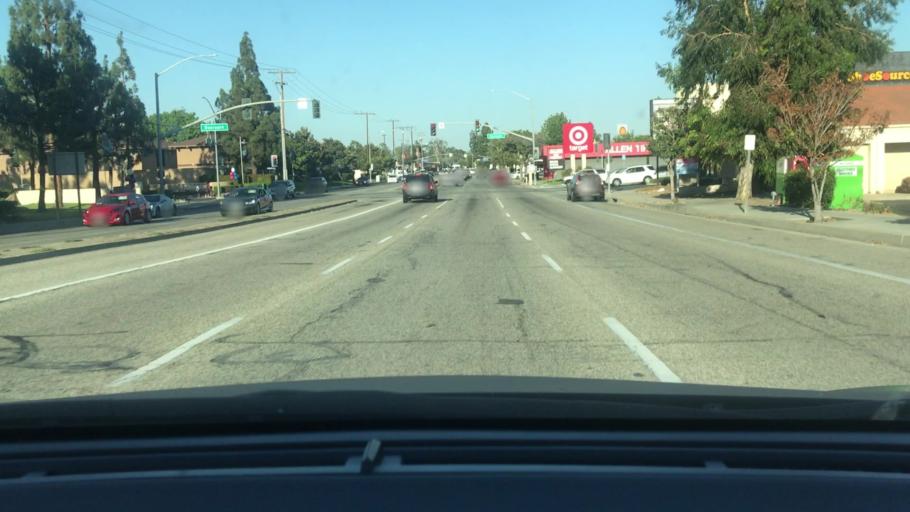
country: US
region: California
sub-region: Orange County
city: Placentia
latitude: 33.8890
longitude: -117.8777
